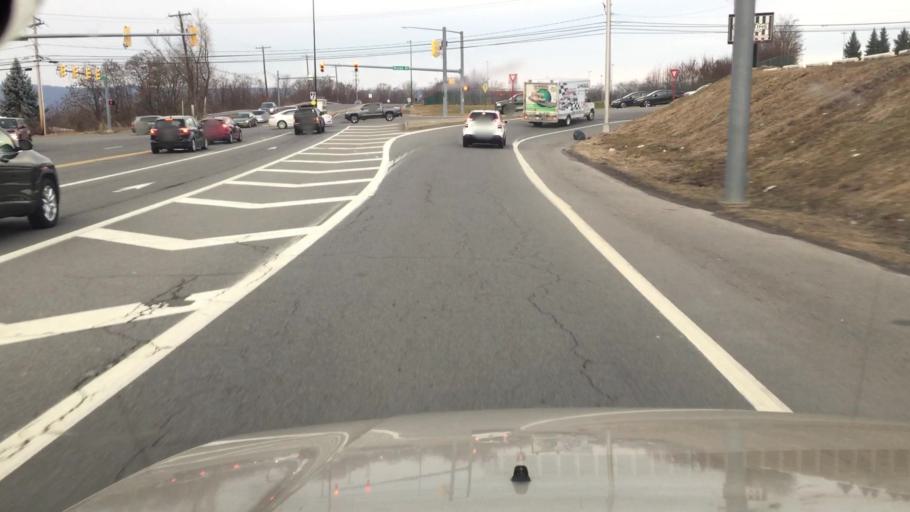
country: US
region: Pennsylvania
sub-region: Luzerne County
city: Georgetown
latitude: 41.2431
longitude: -75.8491
